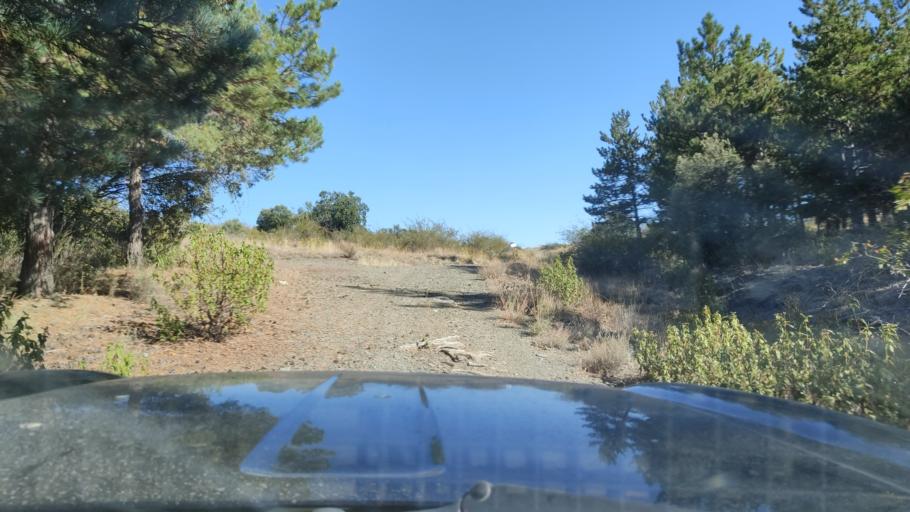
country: ES
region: Aragon
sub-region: Provincia de Teruel
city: Monforte de Moyuela
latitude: 41.0208
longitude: -1.0078
